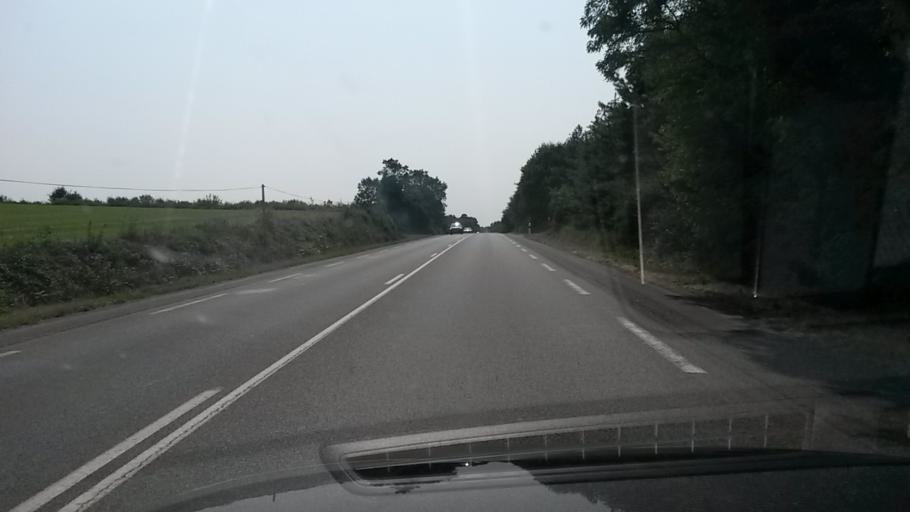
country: FR
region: Pays de la Loire
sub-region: Departement de la Mayenne
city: Chateau-Gontier
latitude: 47.8605
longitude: -0.6912
